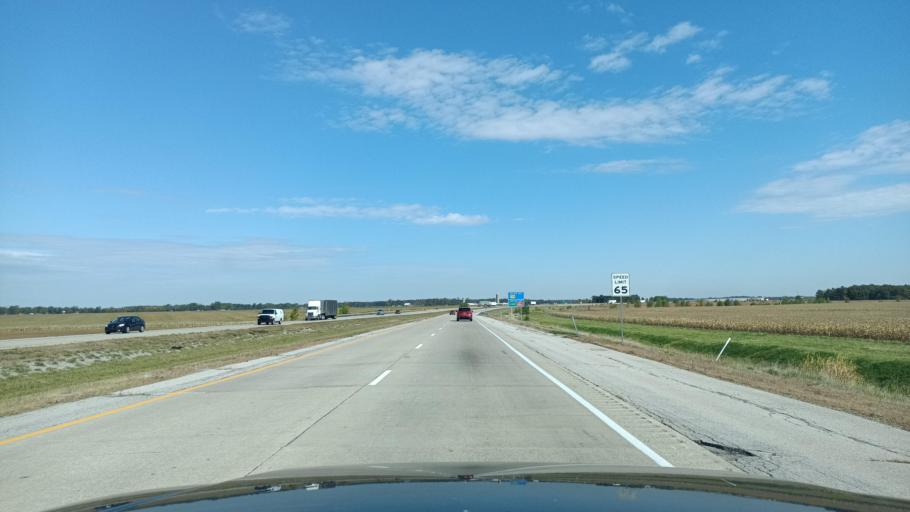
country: US
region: Indiana
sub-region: Allen County
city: Woodburn
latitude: 41.1295
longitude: -84.8779
